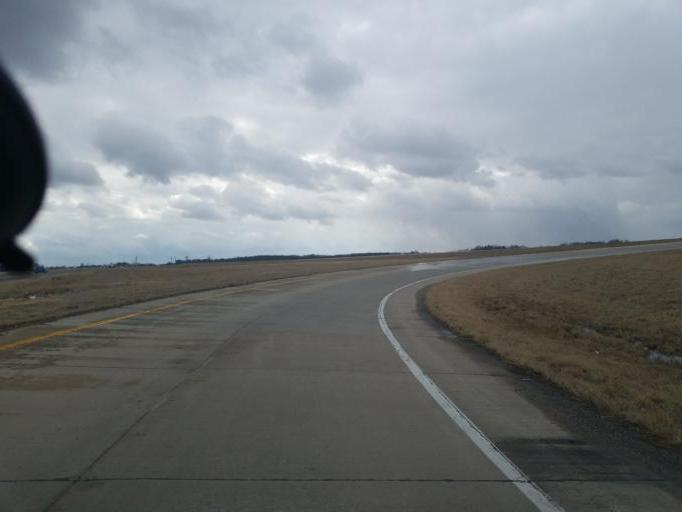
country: US
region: Missouri
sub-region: Boone County
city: Hallsville
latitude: 39.2447
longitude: -92.3243
